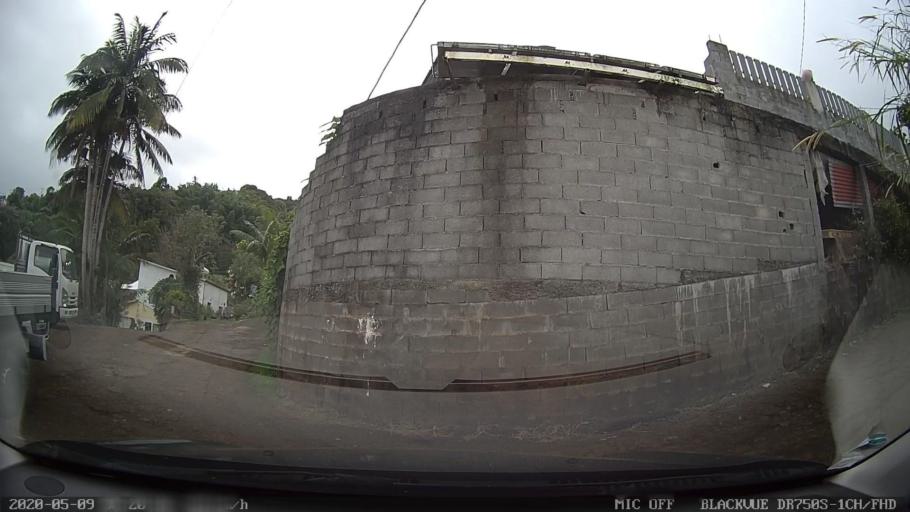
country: RE
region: Reunion
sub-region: Reunion
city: Sainte-Marie
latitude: -20.9504
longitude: 55.5317
